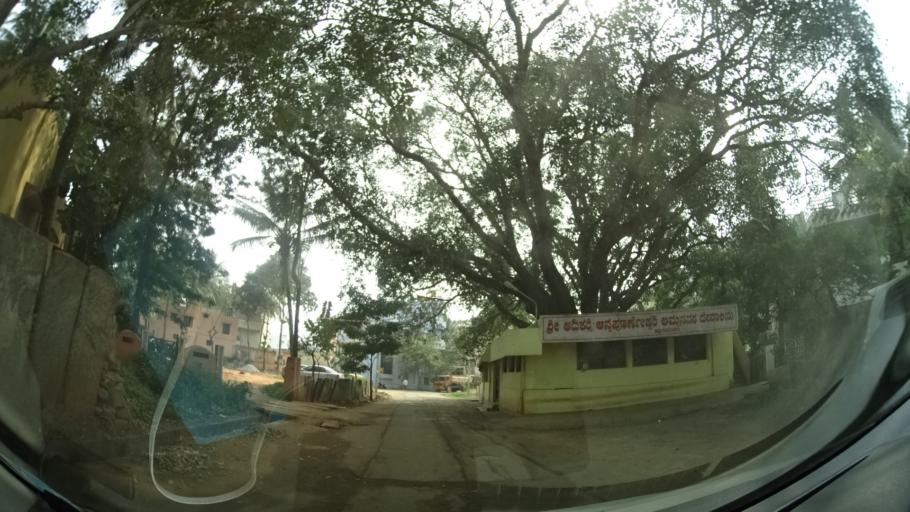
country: IN
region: Karnataka
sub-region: Bangalore Rural
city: Hoskote
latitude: 12.9666
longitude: 77.7560
